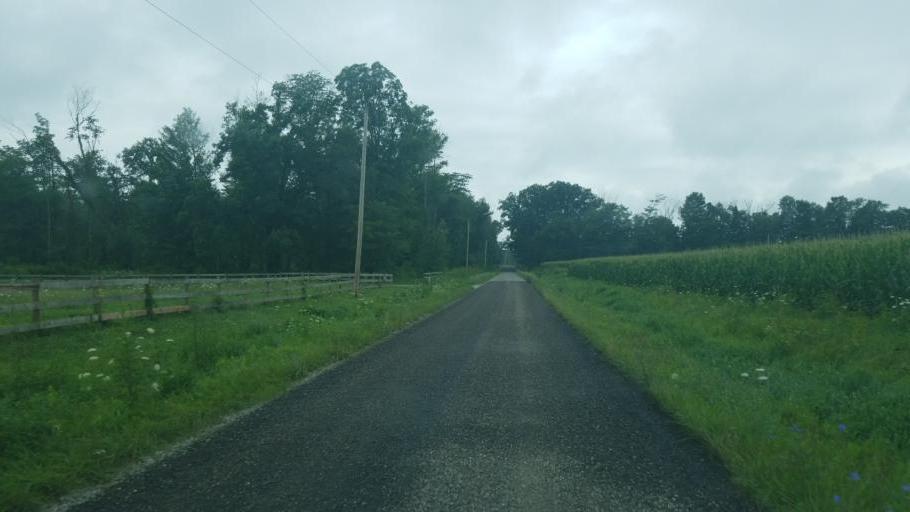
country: US
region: Ohio
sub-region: Knox County
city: Centerburg
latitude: 40.3800
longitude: -82.7496
